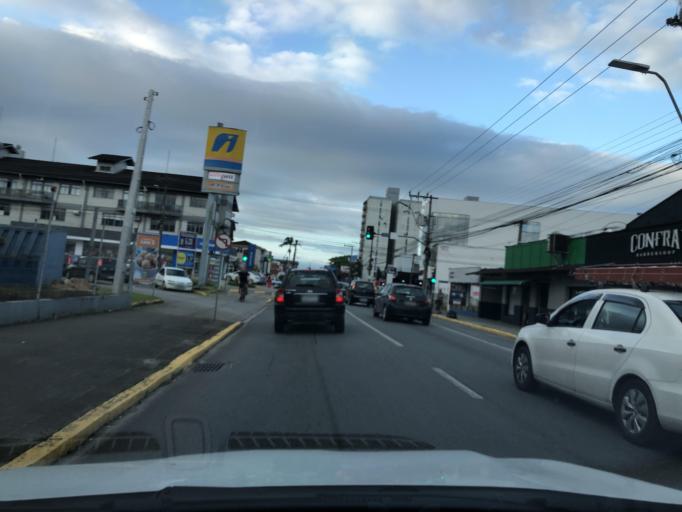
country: BR
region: Santa Catarina
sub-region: Joinville
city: Joinville
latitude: -26.2847
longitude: -48.8491
